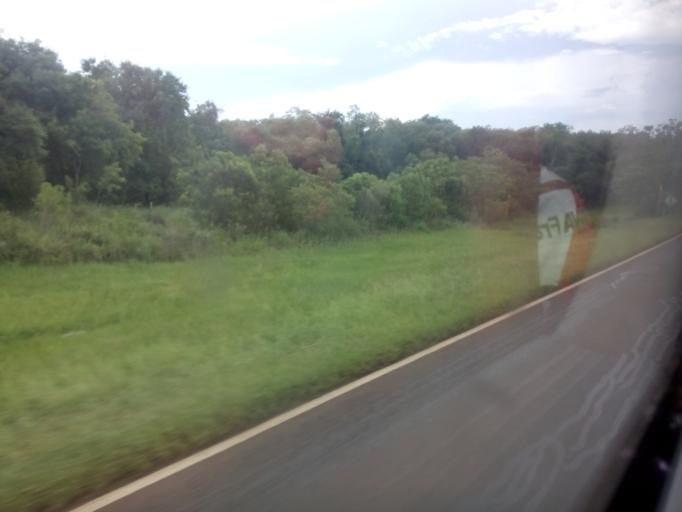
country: AR
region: Misiones
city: Santa Ana
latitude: -27.4231
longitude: -55.6192
